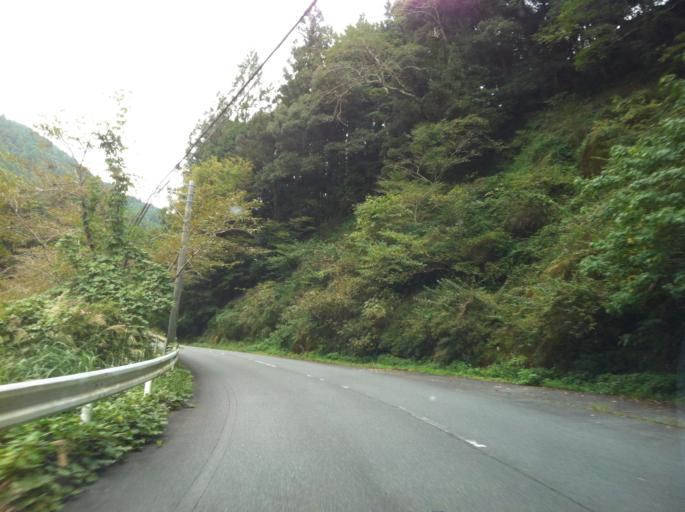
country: JP
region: Shizuoka
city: Mori
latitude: 34.8711
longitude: 138.0177
